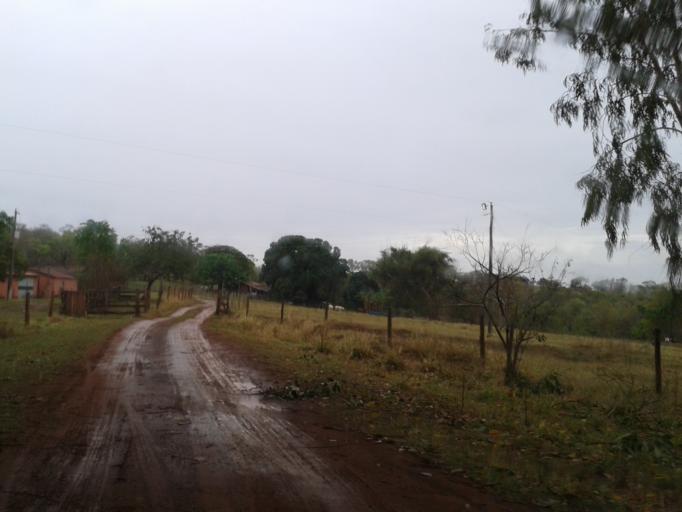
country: BR
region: Minas Gerais
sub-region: Campina Verde
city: Campina Verde
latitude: -19.3134
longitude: -49.5084
